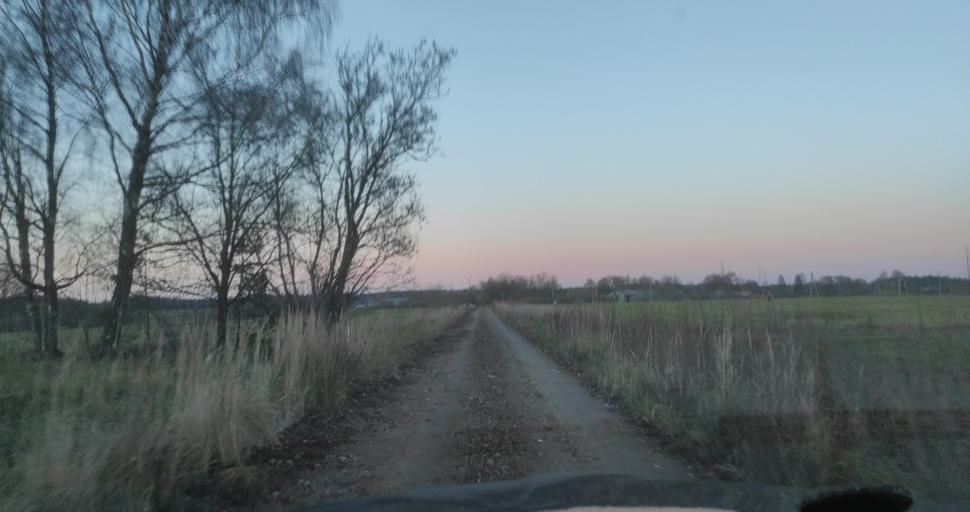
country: LV
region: Dundaga
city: Dundaga
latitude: 57.3716
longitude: 22.2246
